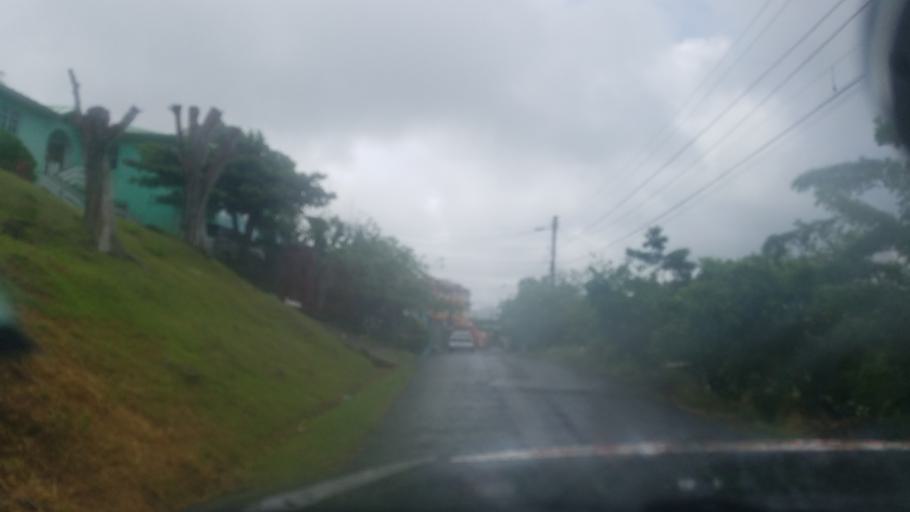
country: LC
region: Laborie Quarter
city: Laborie
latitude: 13.7477
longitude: -60.9676
